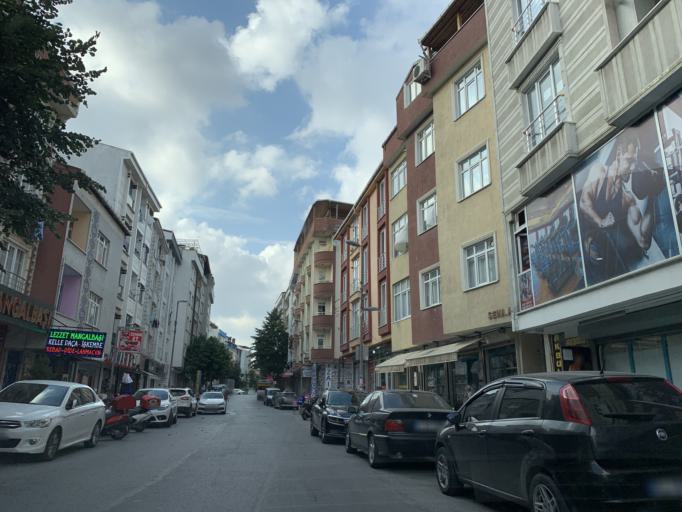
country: TR
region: Istanbul
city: Esenyurt
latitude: 41.0266
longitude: 28.6752
